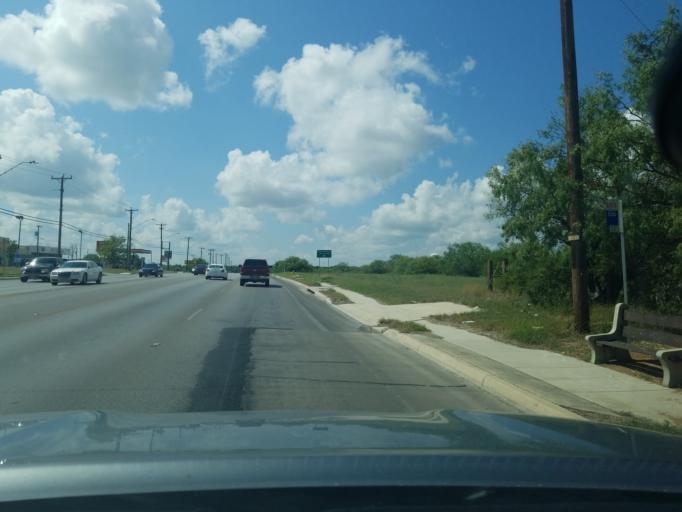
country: US
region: Texas
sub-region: Bexar County
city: San Antonio
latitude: 29.3396
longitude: -98.5342
